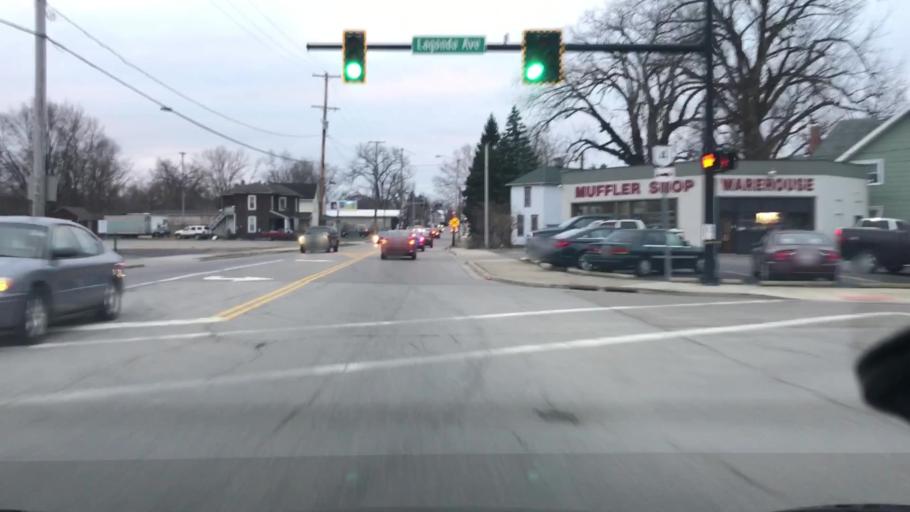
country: US
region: Ohio
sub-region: Clark County
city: Springfield
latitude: 39.9367
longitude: -83.7782
